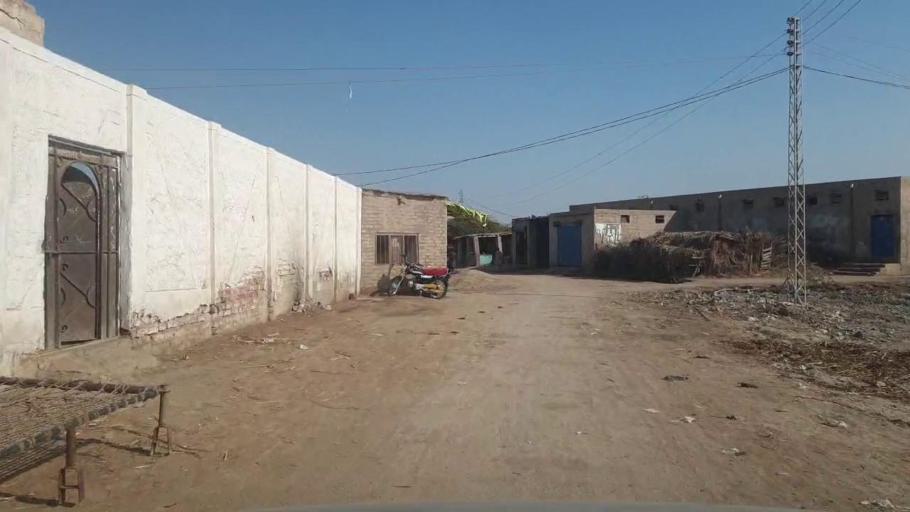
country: PK
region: Sindh
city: Chambar
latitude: 25.2874
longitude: 68.8533
